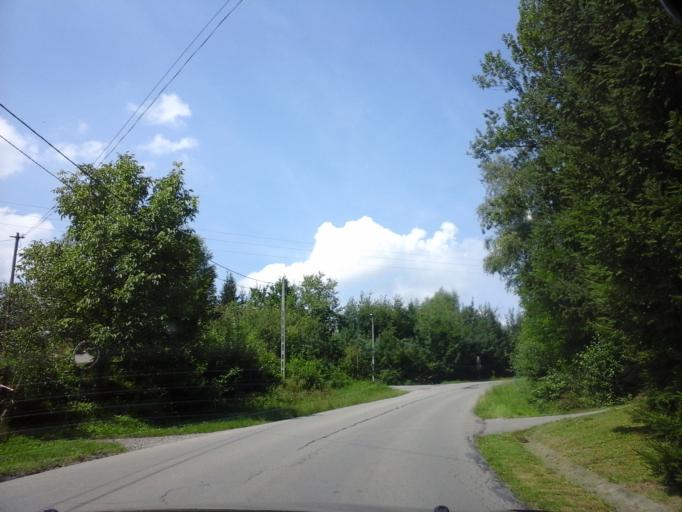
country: PL
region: Lesser Poland Voivodeship
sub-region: Powiat wadowicki
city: Wozniki
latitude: 49.9394
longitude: 19.4921
